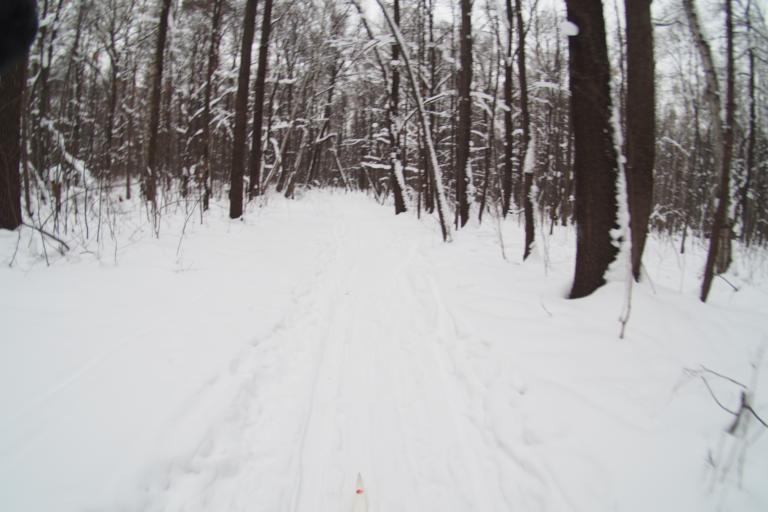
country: RU
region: Moskovskaya
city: Izmaylovo
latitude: 55.7762
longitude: 37.7848
